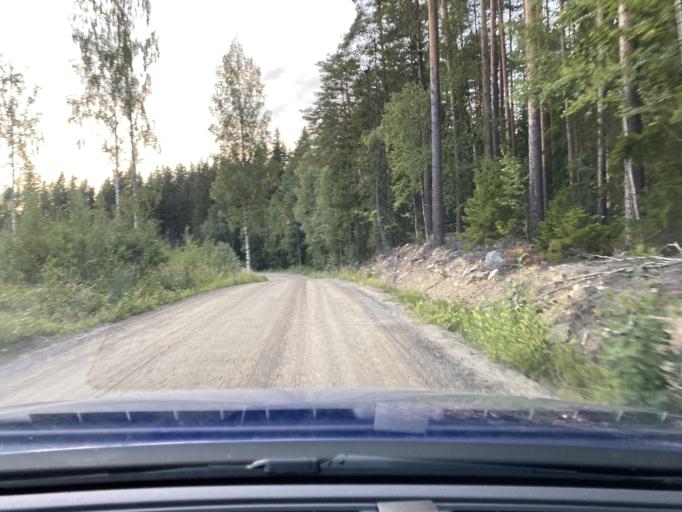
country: FI
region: Pirkanmaa
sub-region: Lounais-Pirkanmaa
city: Punkalaidun
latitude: 61.0621
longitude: 23.2512
